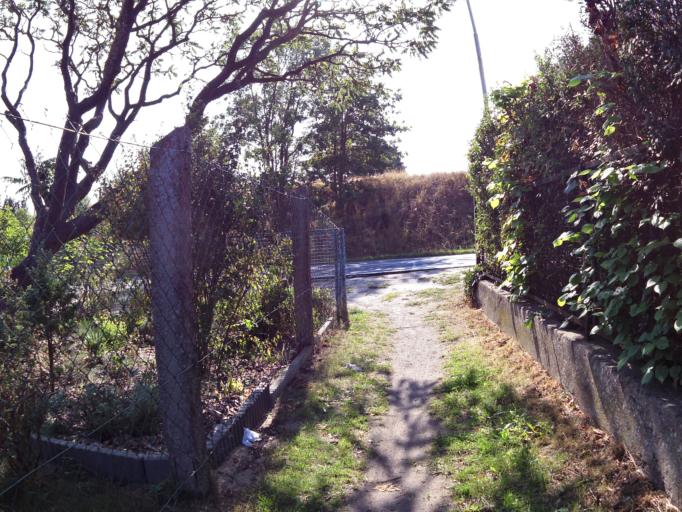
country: DE
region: Mecklenburg-Vorpommern
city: Seebad Bansin
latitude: 53.9684
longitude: 14.0689
